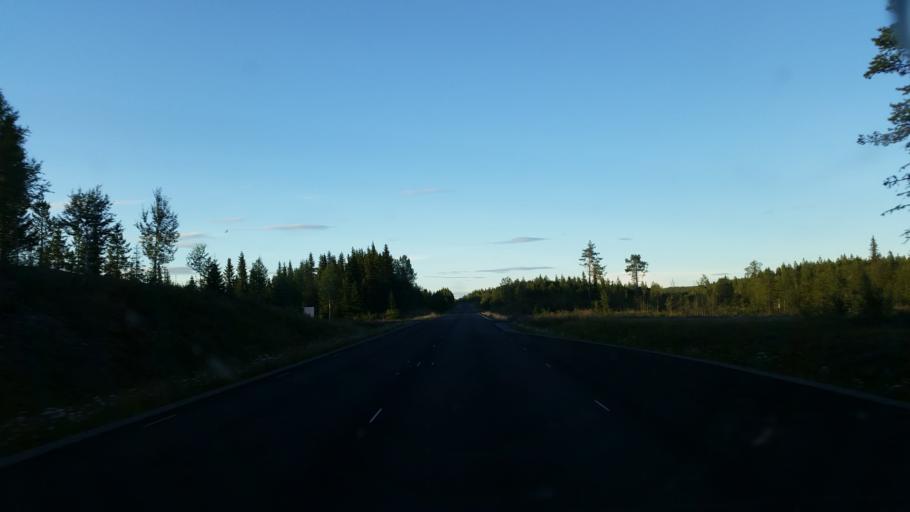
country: SE
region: Vaesterbotten
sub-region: Vilhelmina Kommun
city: Vilhelmina
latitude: 64.7629
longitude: 16.7389
